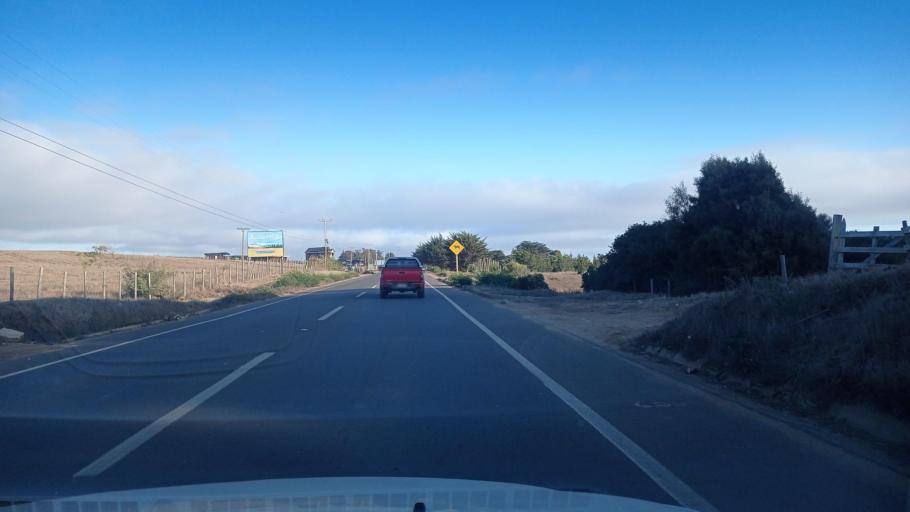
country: CL
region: O'Higgins
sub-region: Provincia de Colchagua
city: Santa Cruz
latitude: -34.4351
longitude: -72.0331
